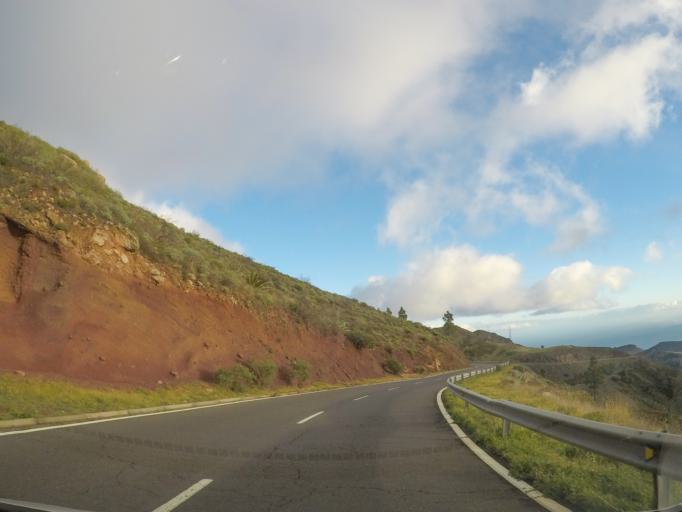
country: ES
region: Canary Islands
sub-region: Provincia de Santa Cruz de Tenerife
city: Alajero
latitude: 28.0863
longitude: -17.2472
